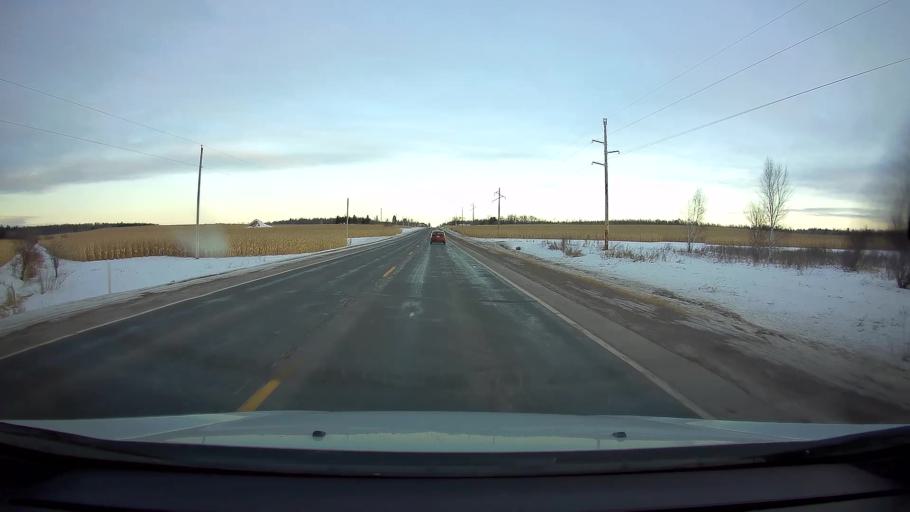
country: US
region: Wisconsin
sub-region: Barron County
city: Turtle Lake
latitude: 45.3464
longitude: -92.1671
